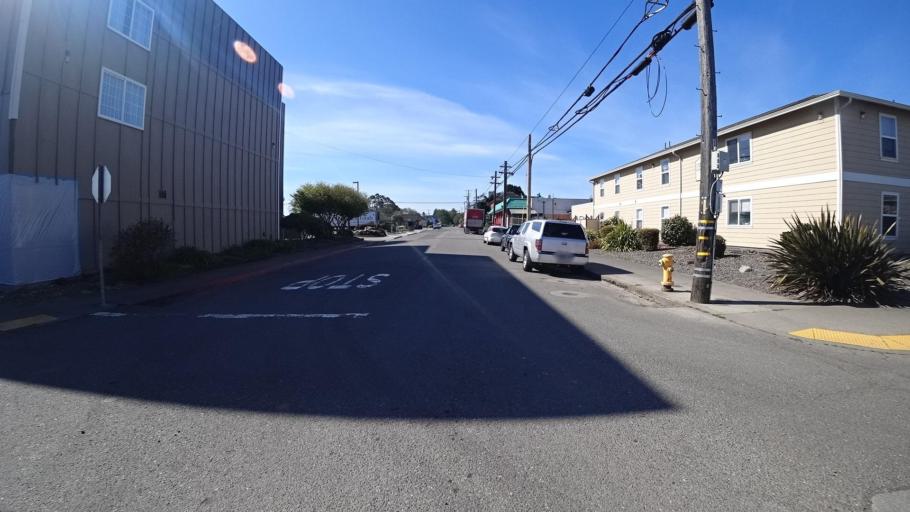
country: US
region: California
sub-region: Humboldt County
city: Eureka
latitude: 40.8055
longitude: -124.1515
